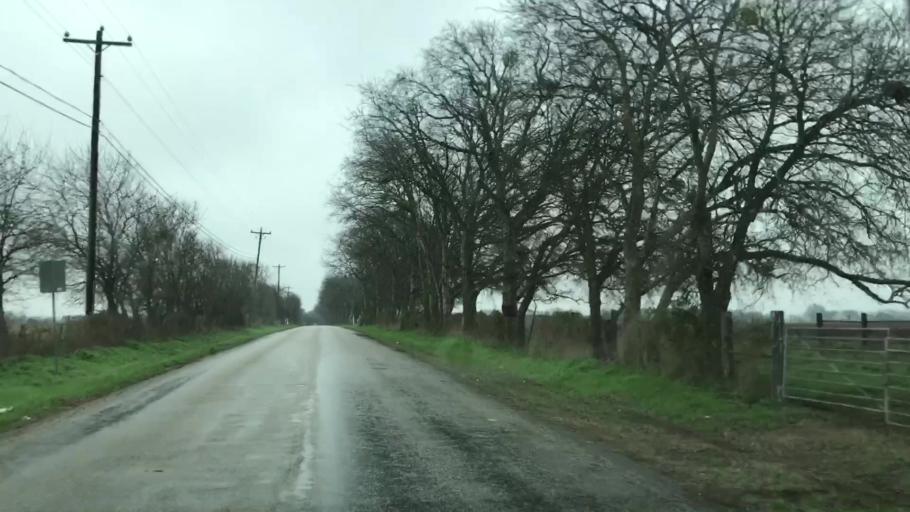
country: US
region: Texas
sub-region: Hays County
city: San Marcos
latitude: 29.8966
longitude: -97.8948
